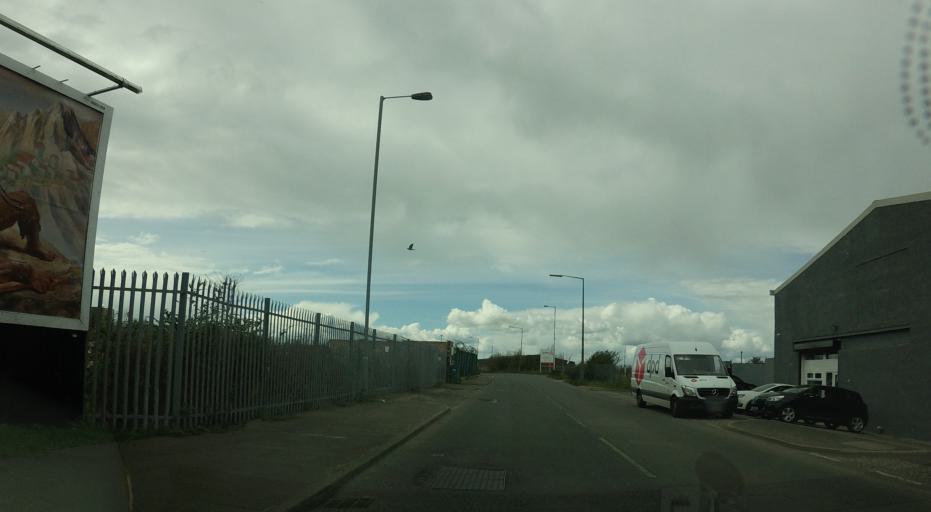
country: GB
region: Scotland
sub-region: Edinburgh
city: Edinburgh
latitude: 55.9830
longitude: -3.2328
